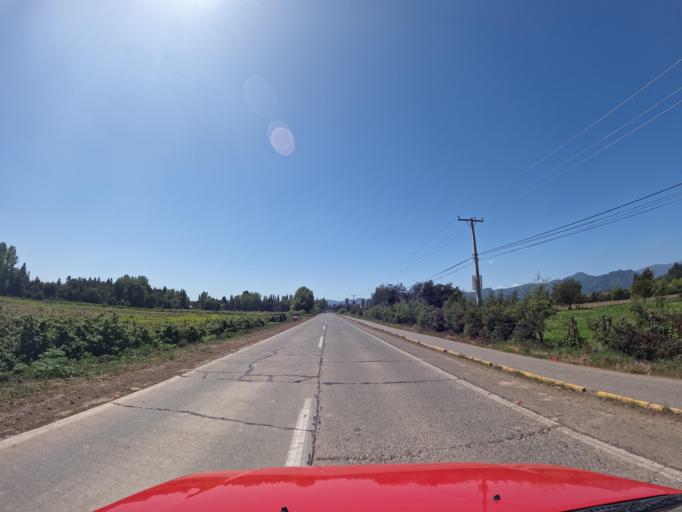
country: CL
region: Maule
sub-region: Provincia de Linares
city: Colbun
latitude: -35.7703
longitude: -71.4272
